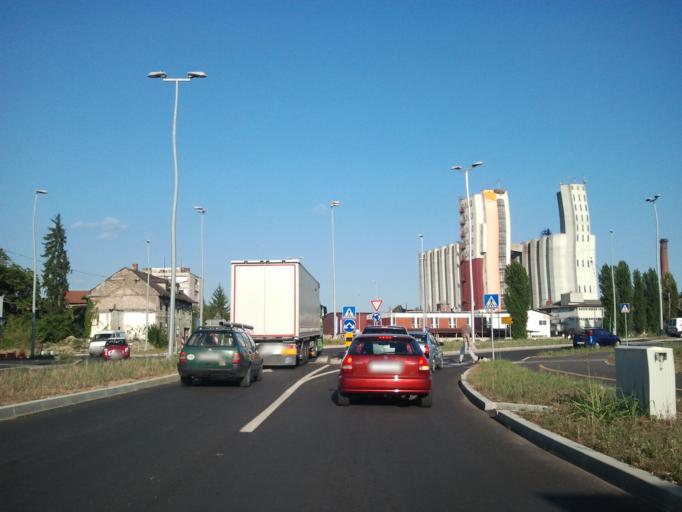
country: HR
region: Sisacko-Moslavacka
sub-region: Grad Sisak
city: Sisak
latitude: 45.4962
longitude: 16.3679
